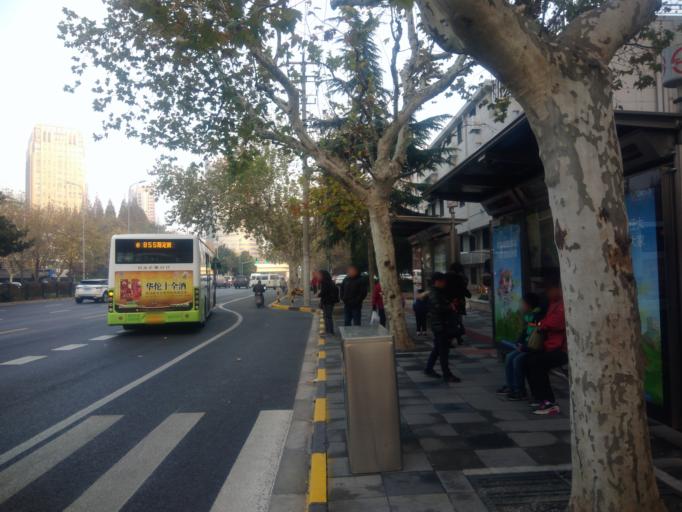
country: CN
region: Shanghai Shi
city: Changning
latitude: 31.1976
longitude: 121.4137
